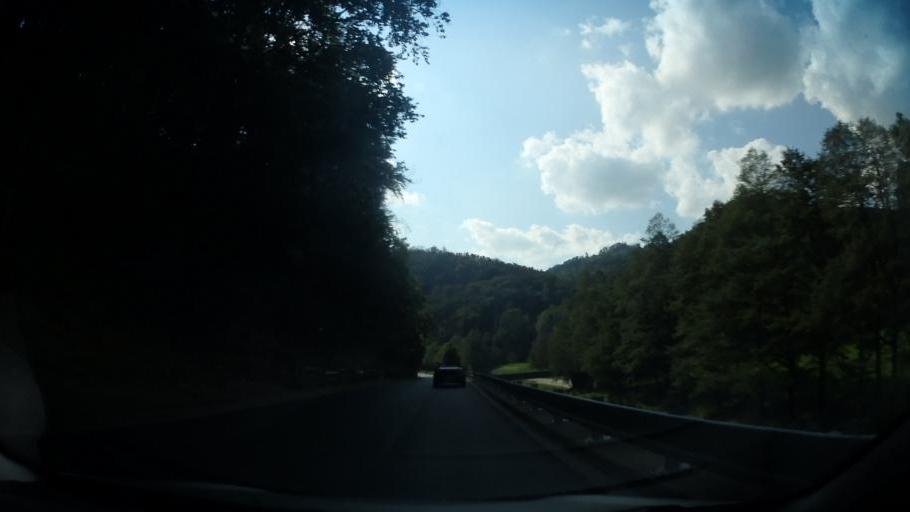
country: CZ
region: South Moravian
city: Olesnice
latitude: 49.5446
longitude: 16.3418
